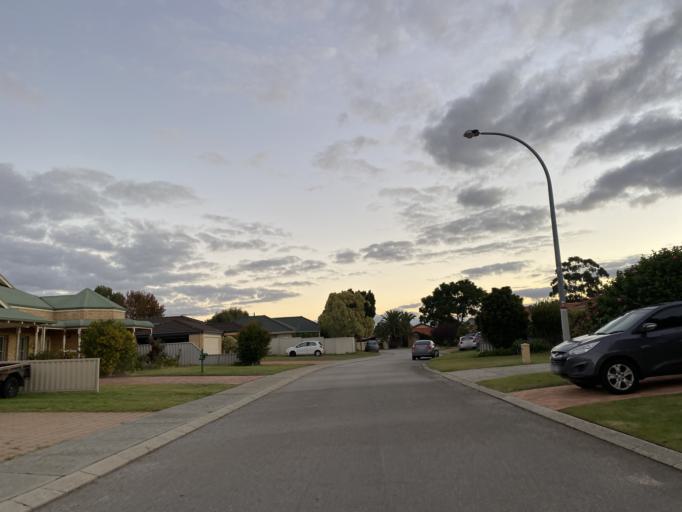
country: AU
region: Western Australia
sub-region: Belmont
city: Kewdale
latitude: -31.9888
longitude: 115.9920
